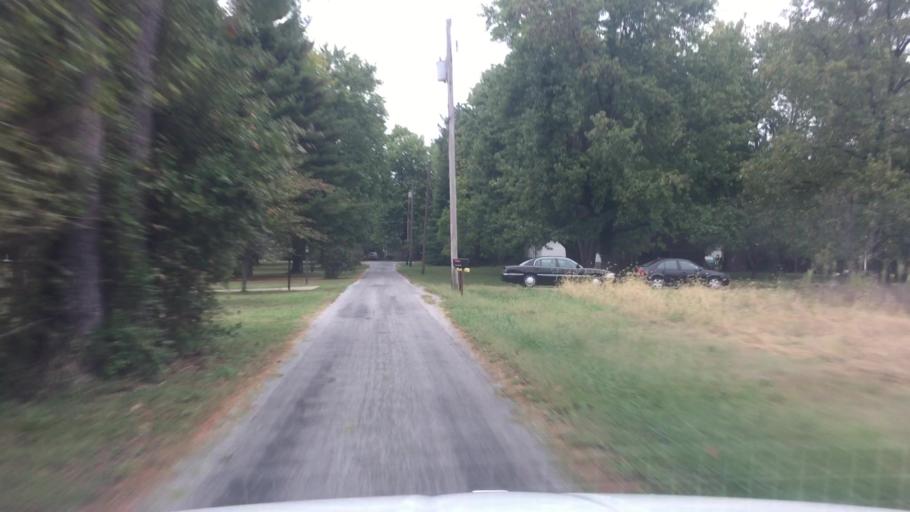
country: US
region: Illinois
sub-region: Franklin County
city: West Frankfort
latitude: 37.8978
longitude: -88.9720
